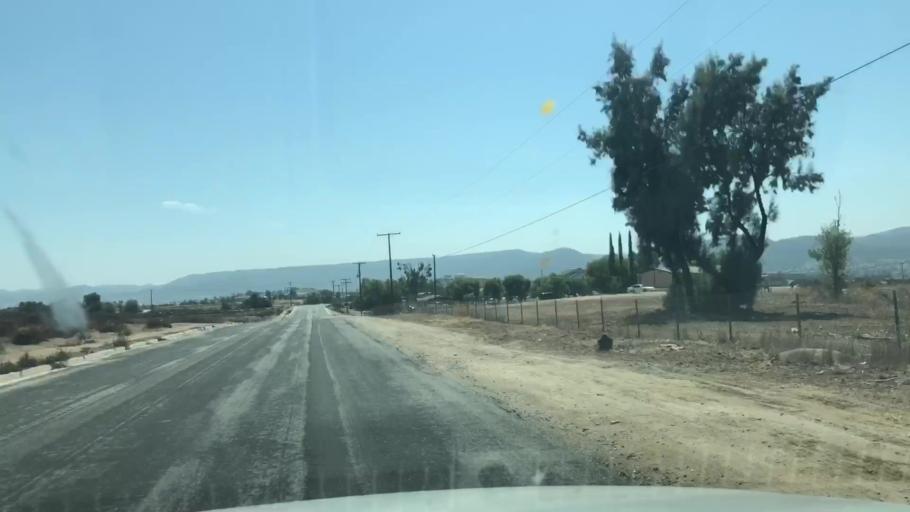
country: US
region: California
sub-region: Riverside County
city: Wildomar
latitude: 33.6005
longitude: -117.2358
